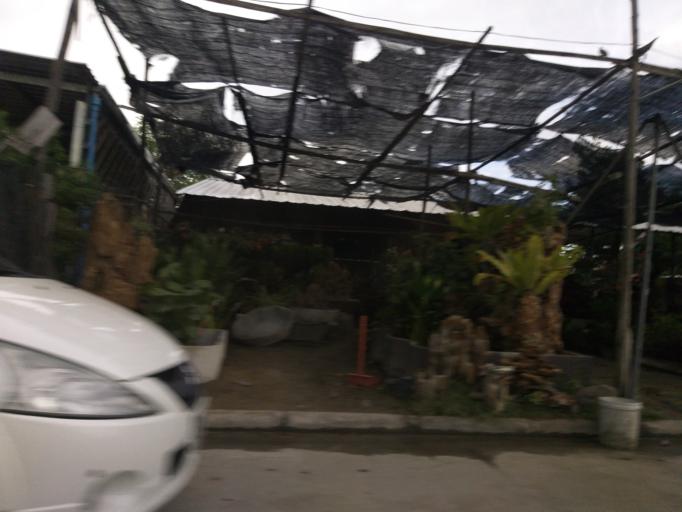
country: TH
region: Nonthaburi
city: Bang Bua Thong
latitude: 13.9339
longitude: 100.4175
